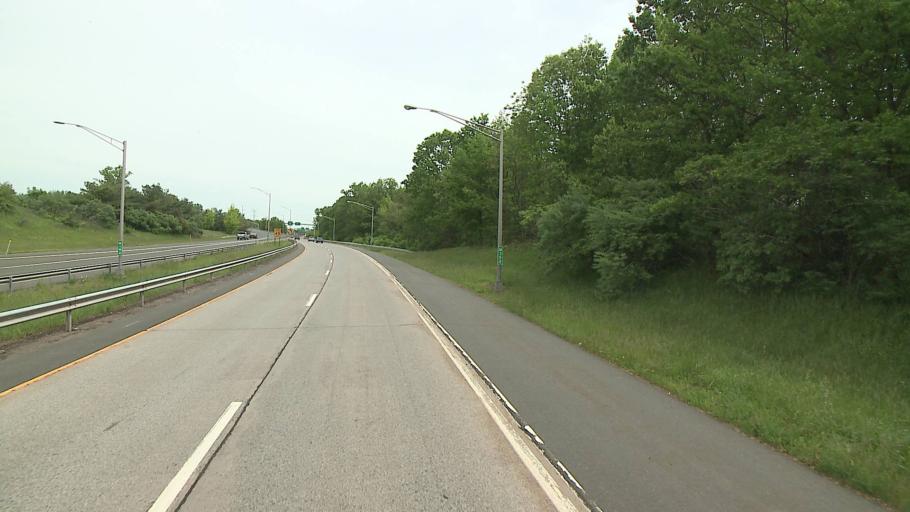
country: US
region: Connecticut
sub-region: Hartford County
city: East Hartford
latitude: 41.7831
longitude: -72.5668
